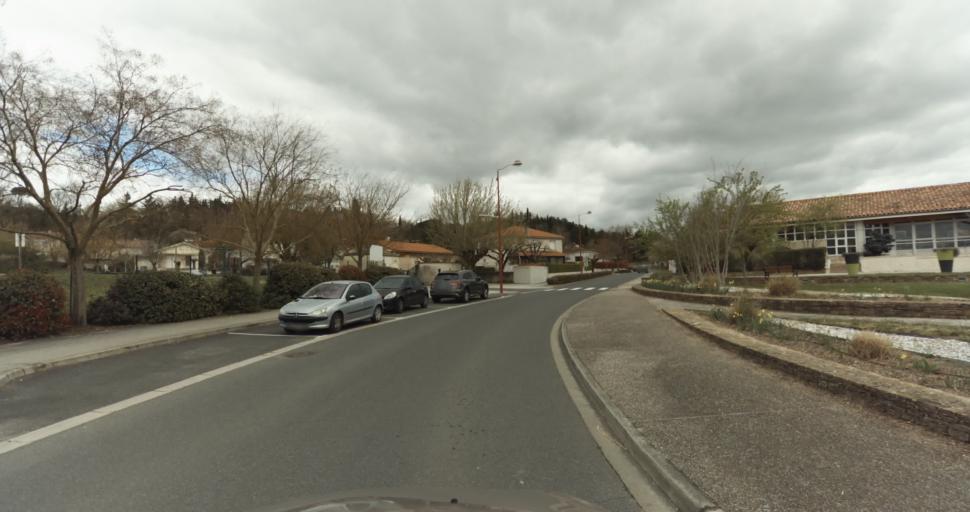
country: FR
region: Midi-Pyrenees
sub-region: Departement du Tarn
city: Puygouzon
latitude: 43.8924
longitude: 2.1694
